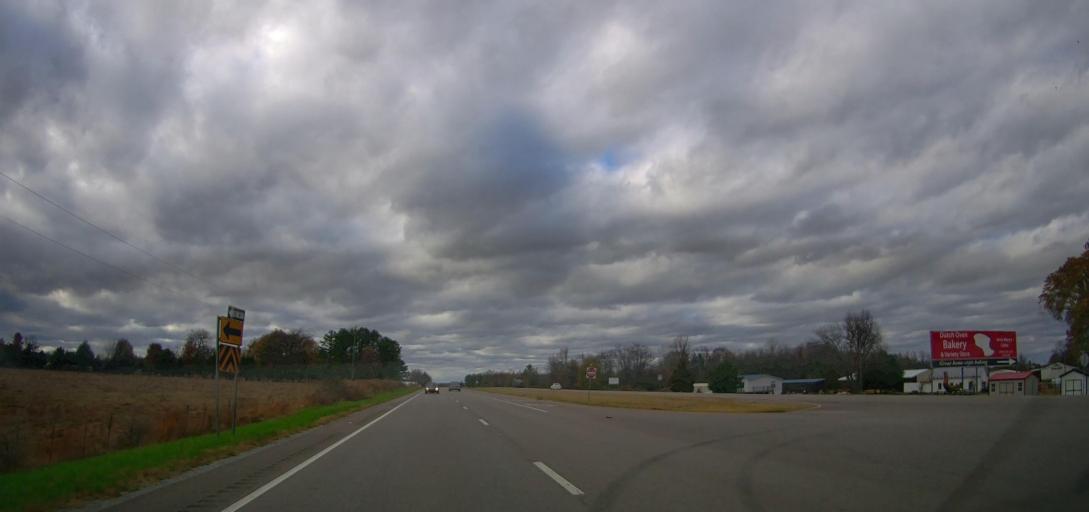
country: US
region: Alabama
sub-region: Morgan County
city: Danville
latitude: 34.3346
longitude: -87.0158
